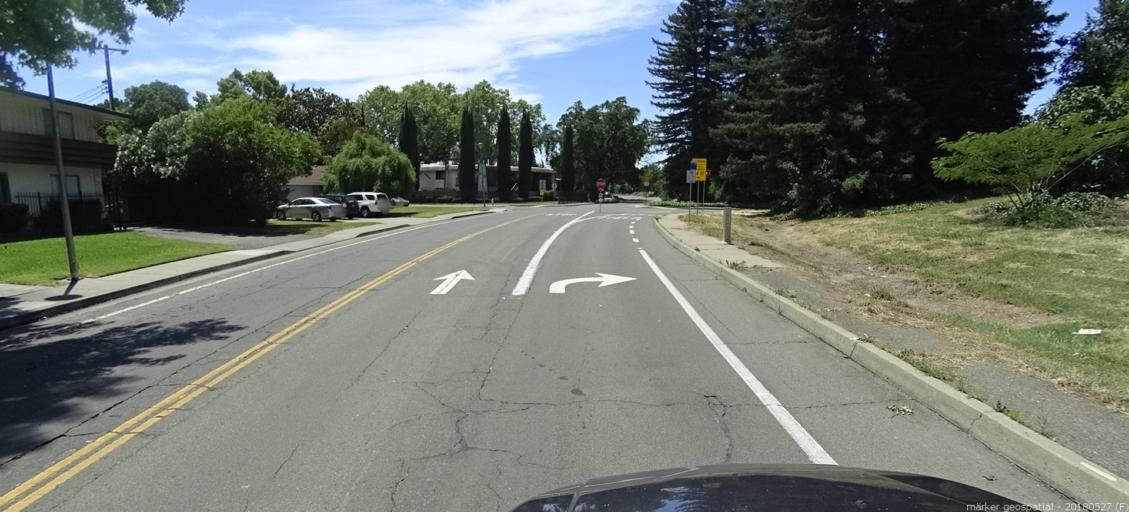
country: US
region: California
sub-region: Yolo County
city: West Sacramento
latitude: 38.5345
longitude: -121.5161
